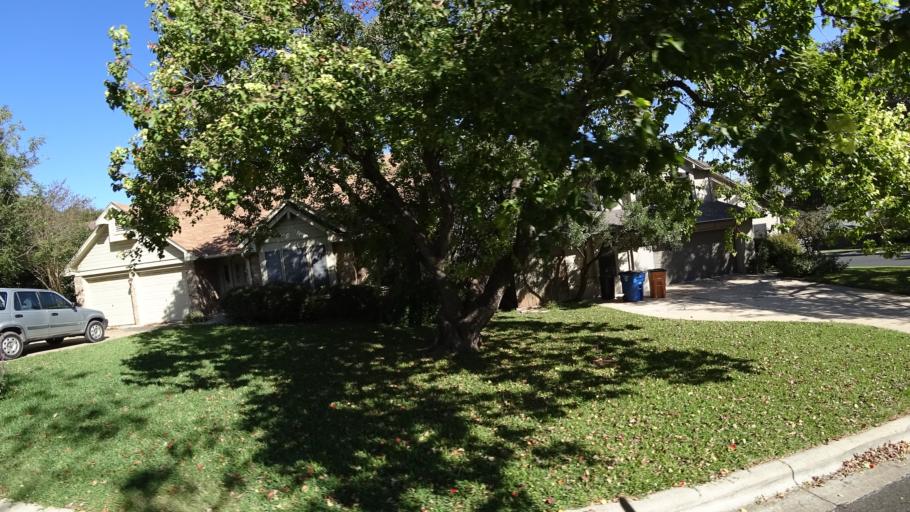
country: US
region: Texas
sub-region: Williamson County
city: Jollyville
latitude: 30.4150
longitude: -97.7596
